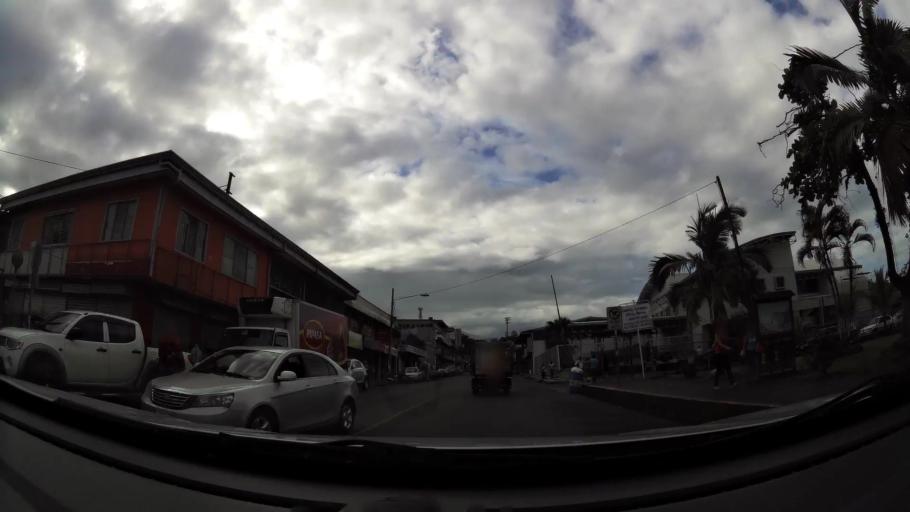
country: CR
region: Limon
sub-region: Canton de Pococi
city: Guapiles
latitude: 10.2136
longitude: -83.7890
